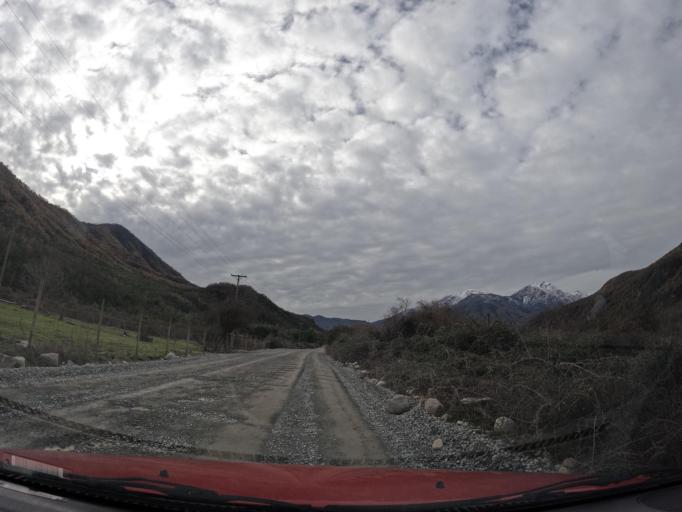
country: CL
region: Maule
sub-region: Provincia de Linares
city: Colbun
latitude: -35.8849
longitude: -71.2771
